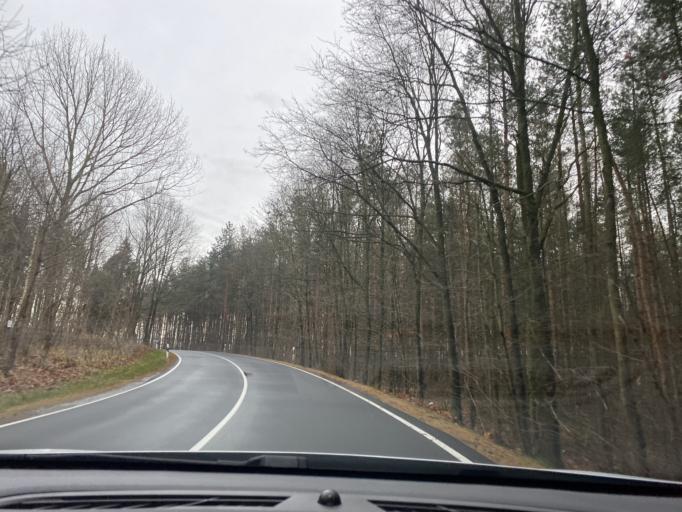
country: DE
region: Saxony
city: Reichenbach
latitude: 51.1135
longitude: 14.8393
